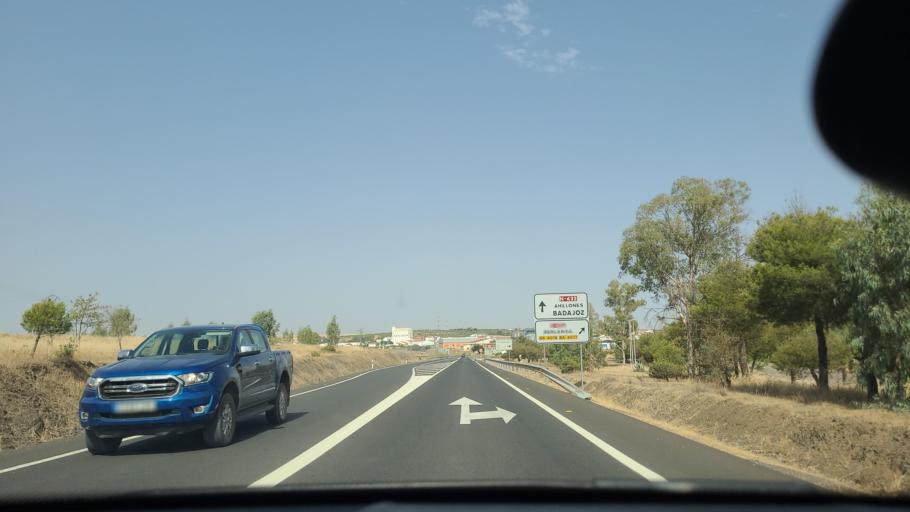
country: ES
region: Extremadura
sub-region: Provincia de Badajoz
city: Berlanga
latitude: 38.2741
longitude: -5.8180
